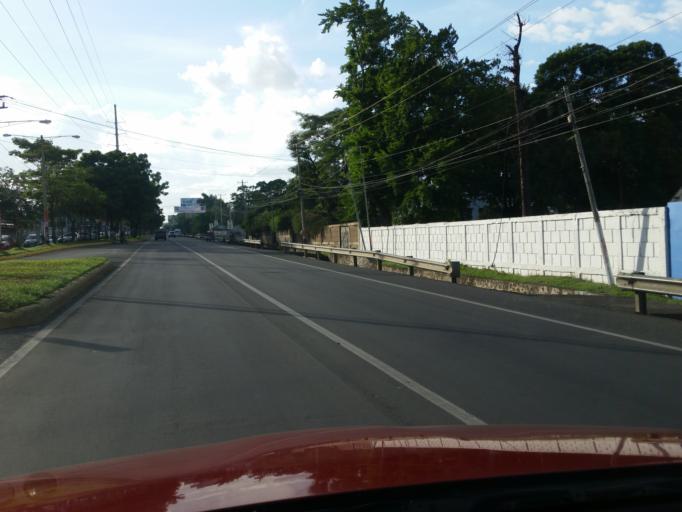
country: NI
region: Masaya
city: Ticuantepe
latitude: 12.0638
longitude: -86.2102
